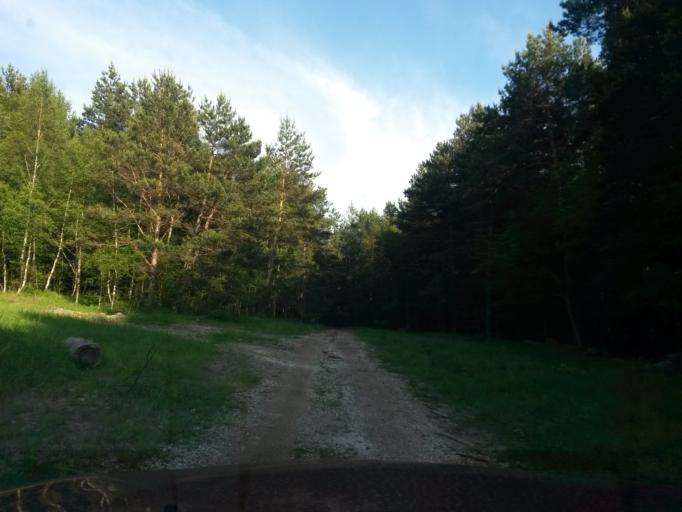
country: SK
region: Kosicky
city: Moldava nad Bodvou
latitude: 48.7428
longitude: 21.0283
